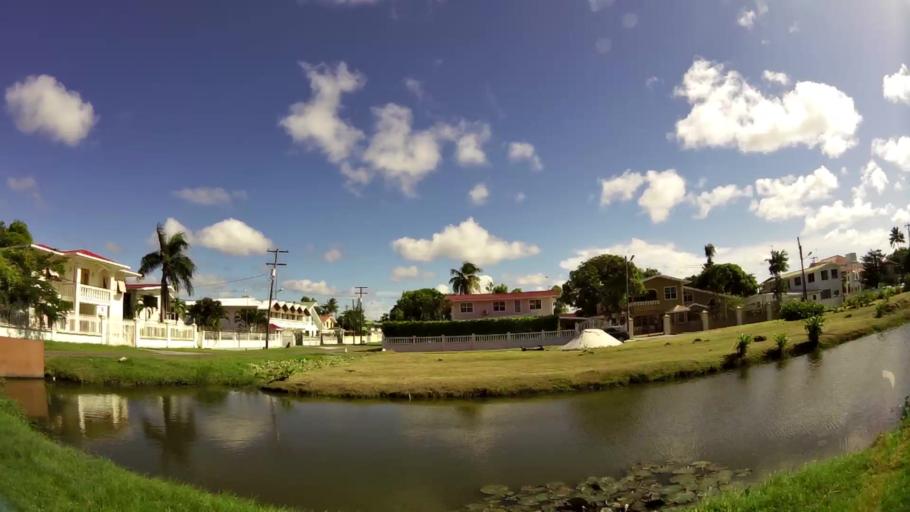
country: GY
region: Demerara-Mahaica
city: Georgetown
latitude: 6.8208
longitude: -58.1278
